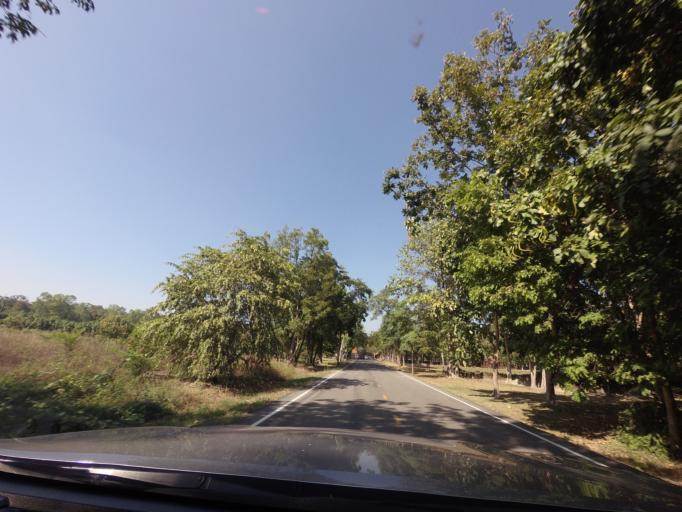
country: TH
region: Sukhothai
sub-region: Amphoe Si Satchanalai
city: Si Satchanalai
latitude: 17.4241
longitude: 99.7886
